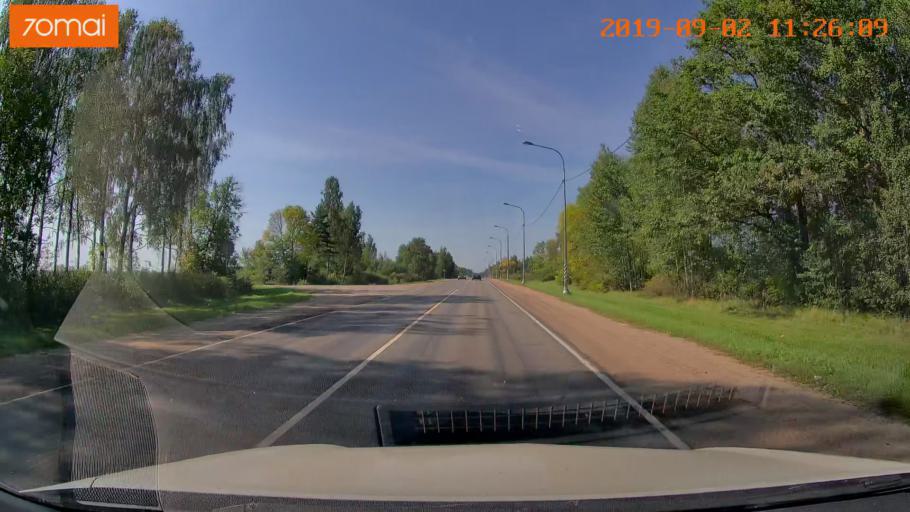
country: RU
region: Smolensk
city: Roslavl'
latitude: 53.9948
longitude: 32.9368
